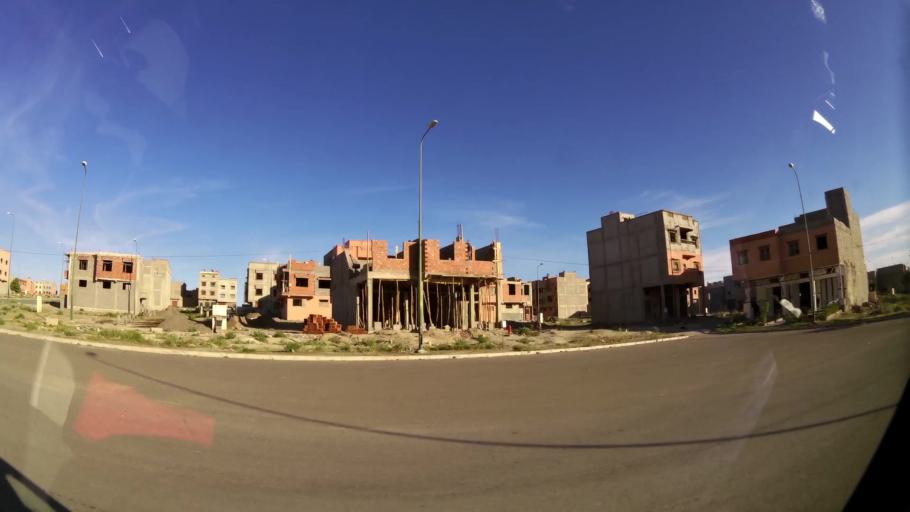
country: MA
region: Marrakech-Tensift-Al Haouz
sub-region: Marrakech
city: Marrakesh
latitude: 31.7674
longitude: -8.0999
